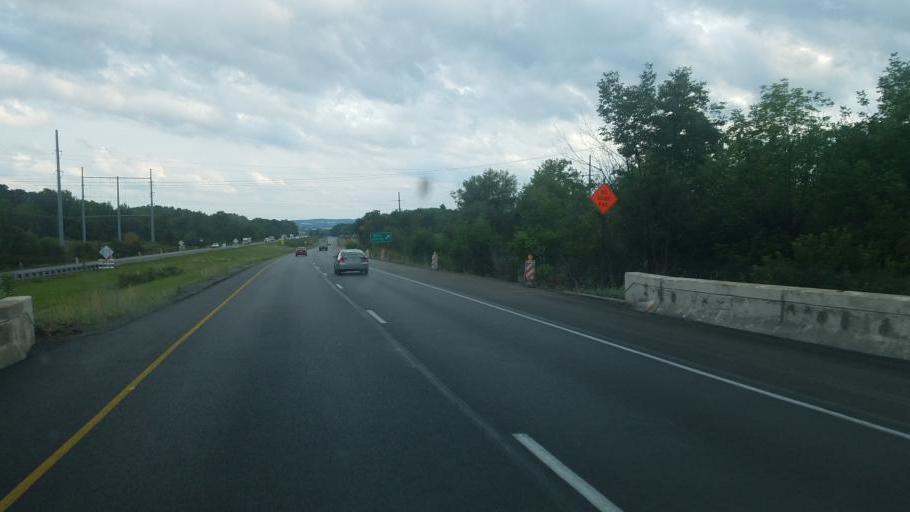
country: US
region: Pennsylvania
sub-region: Butler County
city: Fox Run
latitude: 40.7240
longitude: -80.1019
